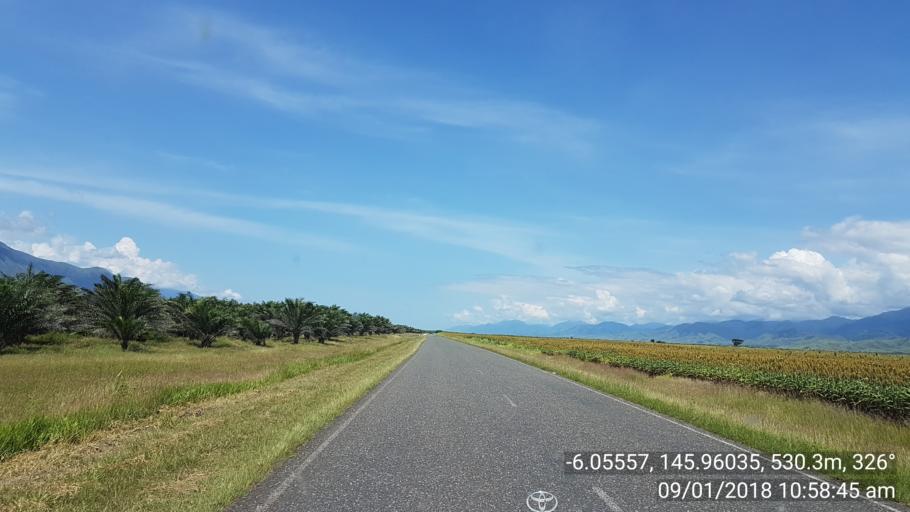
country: PG
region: Eastern Highlands
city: Kainantu
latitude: -6.0560
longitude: 145.9608
